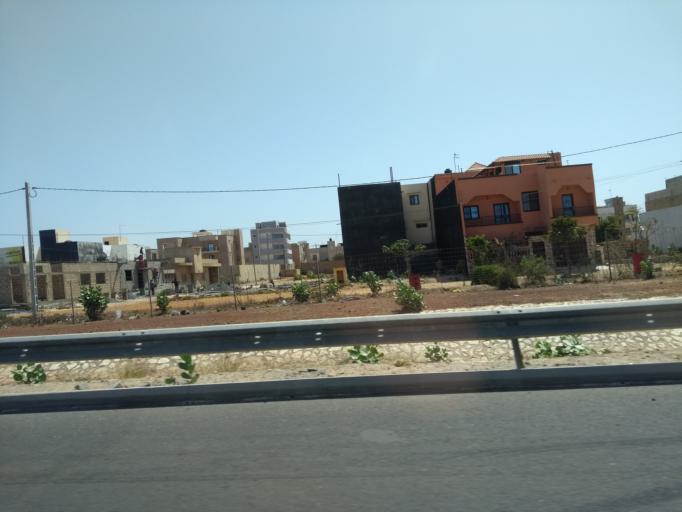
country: SN
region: Dakar
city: Pikine
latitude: 14.7500
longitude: -17.2940
